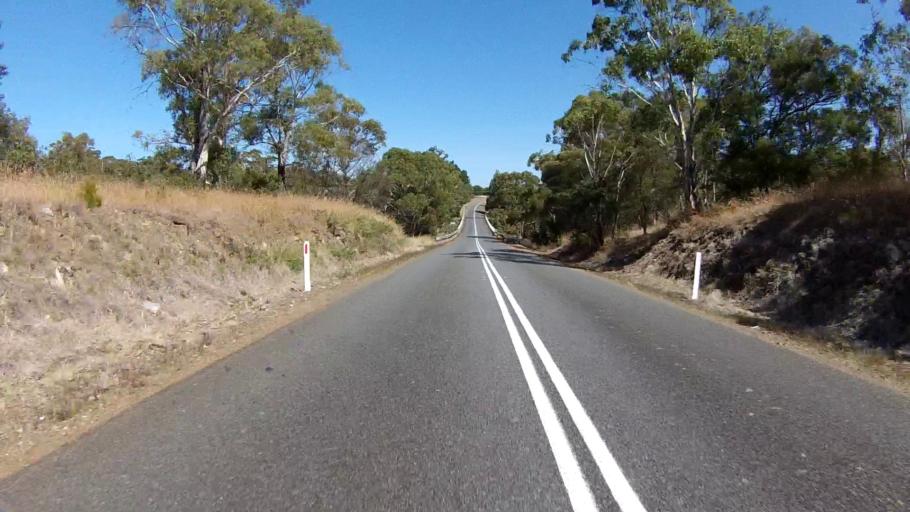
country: AU
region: Tasmania
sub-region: Sorell
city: Sorell
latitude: -42.2839
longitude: 147.9980
